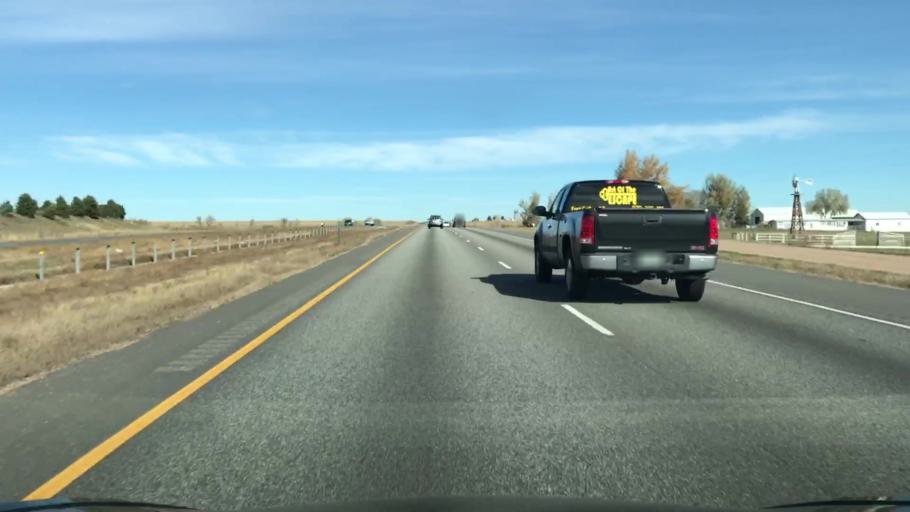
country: US
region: Colorado
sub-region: Weld County
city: Mead
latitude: 40.2517
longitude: -104.9801
